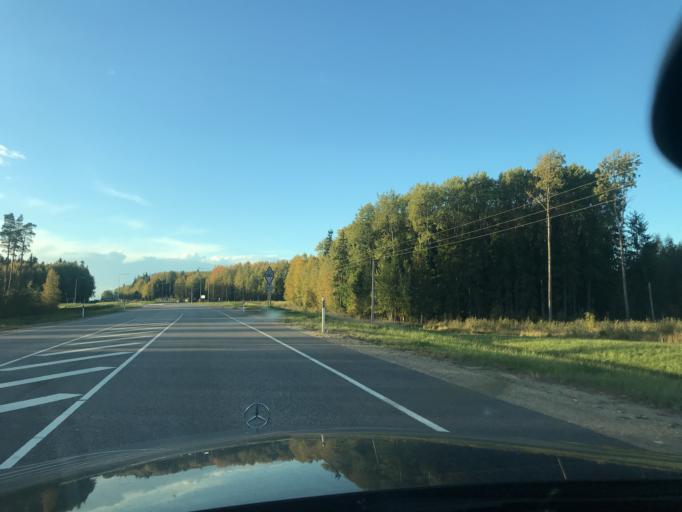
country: EE
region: Vorumaa
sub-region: Voru linn
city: Voru
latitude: 57.8476
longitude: 27.0414
